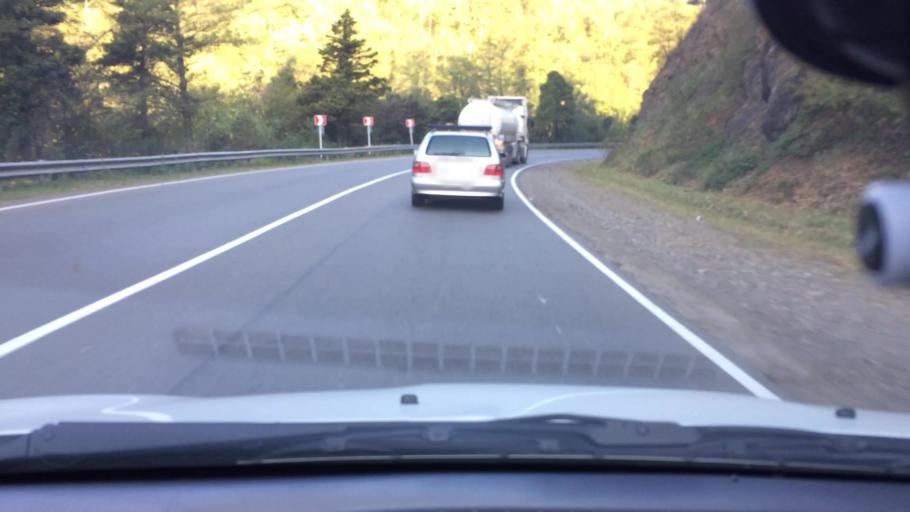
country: GE
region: Imereti
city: Kharagauli
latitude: 42.1078
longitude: 43.2036
